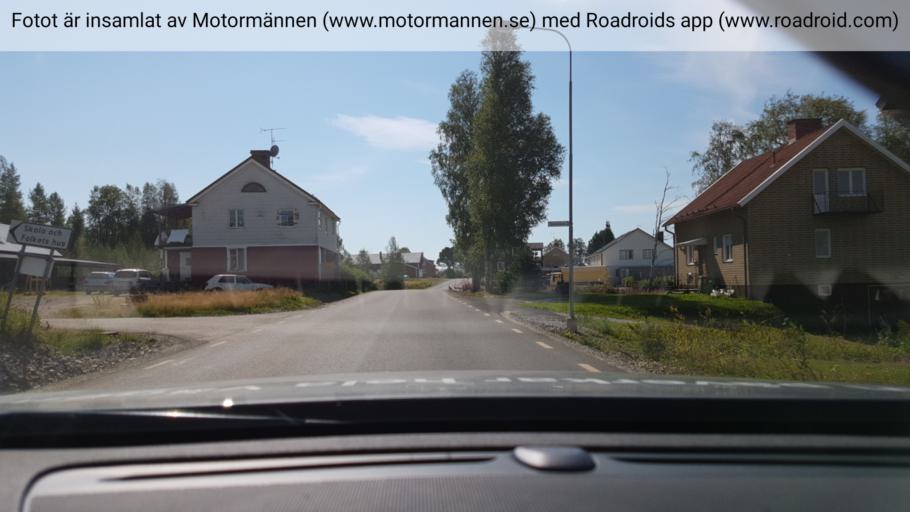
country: SE
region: Vaesterbotten
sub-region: Norsjo Kommun
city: Norsjoe
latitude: 64.5324
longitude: 19.3468
